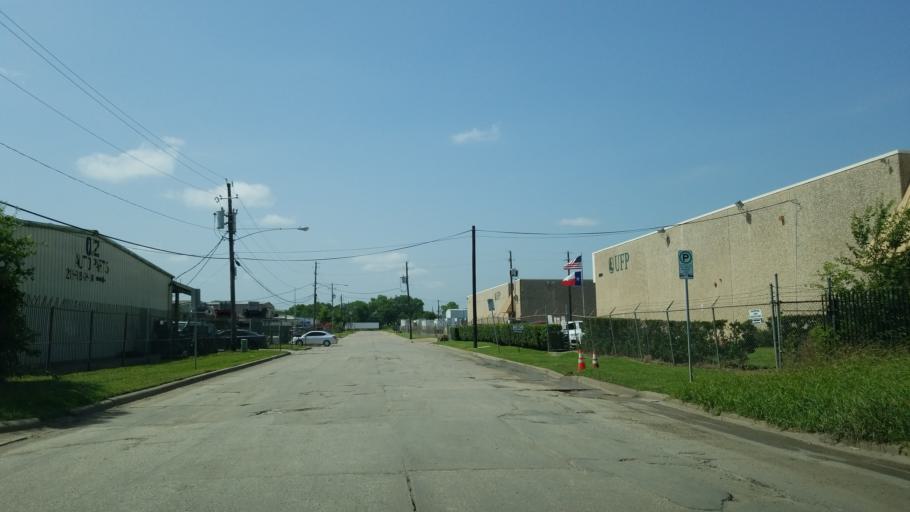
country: US
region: Texas
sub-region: Dallas County
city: Irving
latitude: 32.7778
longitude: -96.9221
